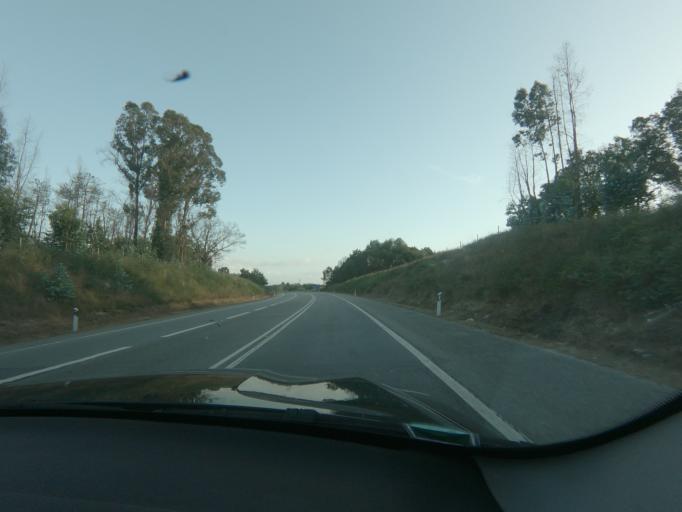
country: PT
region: Viseu
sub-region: Santa Comba Dao
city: Santa Comba Dao
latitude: 40.4214
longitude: -8.1215
